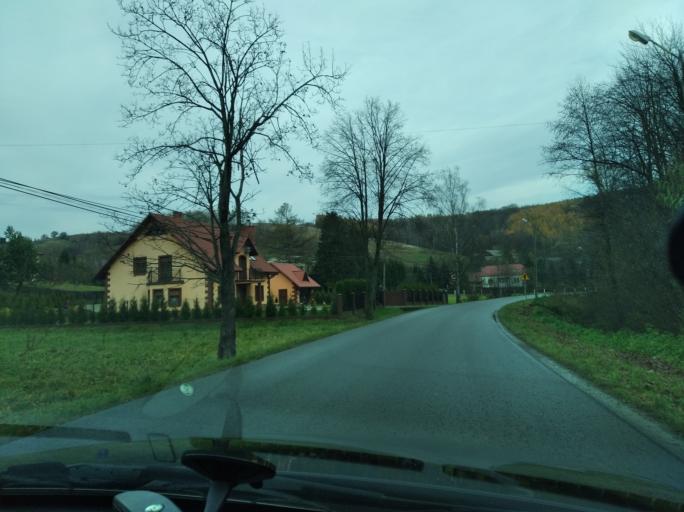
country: PL
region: Subcarpathian Voivodeship
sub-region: Powiat ropczycko-sedziszowski
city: Iwierzyce
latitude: 49.9478
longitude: 21.7469
